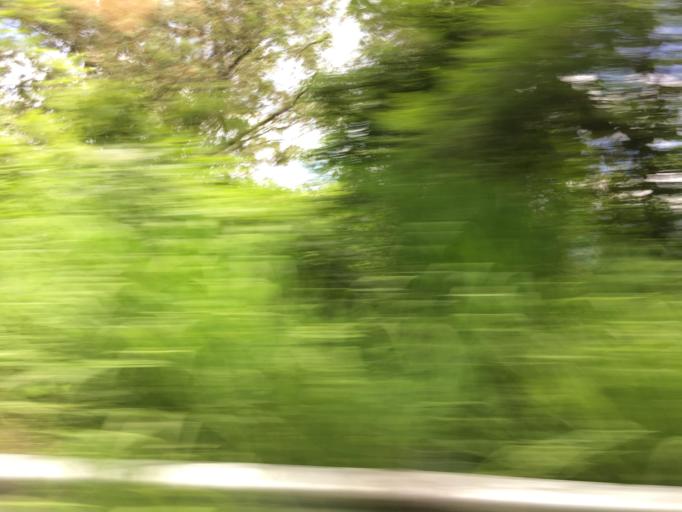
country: GT
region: Guatemala
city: Amatitlan
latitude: 14.4983
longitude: -90.6261
